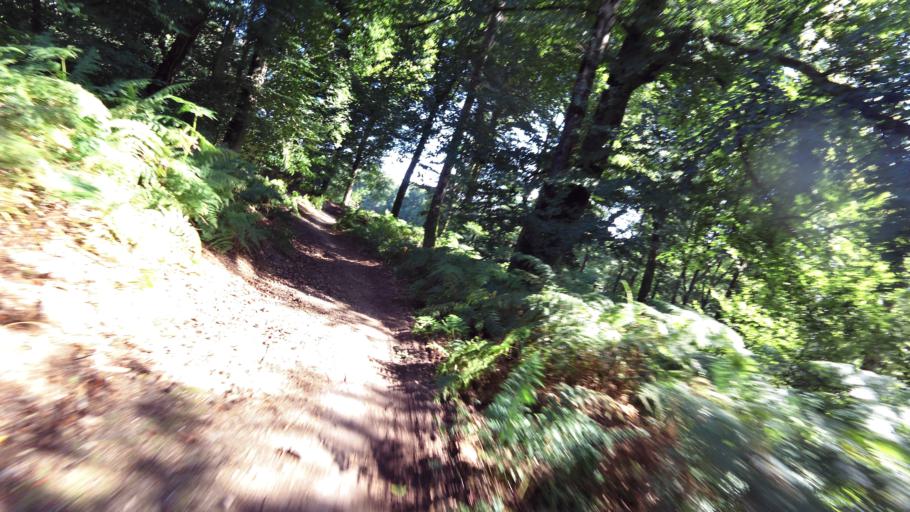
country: NL
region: Gelderland
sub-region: Gemeente Renkum
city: Doorwerth
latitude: 51.9778
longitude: 5.8084
